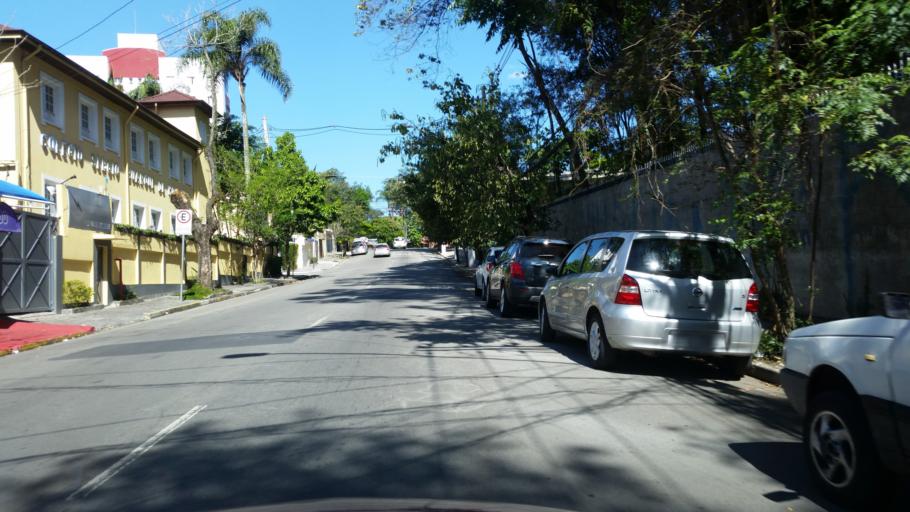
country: BR
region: Sao Paulo
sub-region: Taboao Da Serra
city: Taboao da Serra
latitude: -23.6338
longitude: -46.7047
